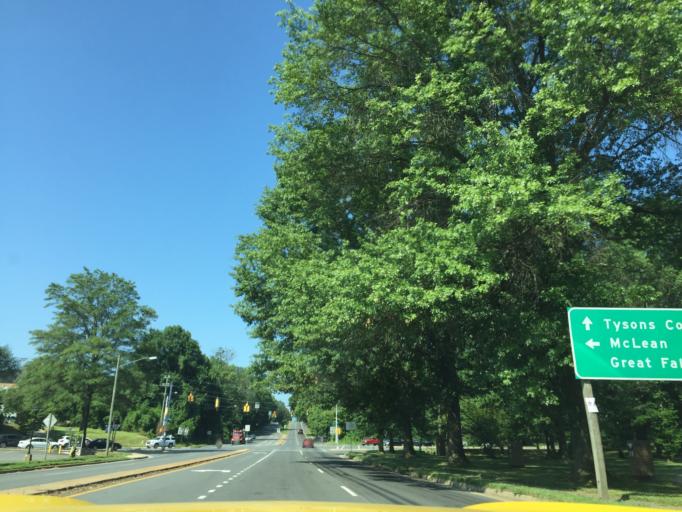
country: US
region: Virginia
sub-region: Fairfax County
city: McLean
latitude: 38.9376
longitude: -77.1842
